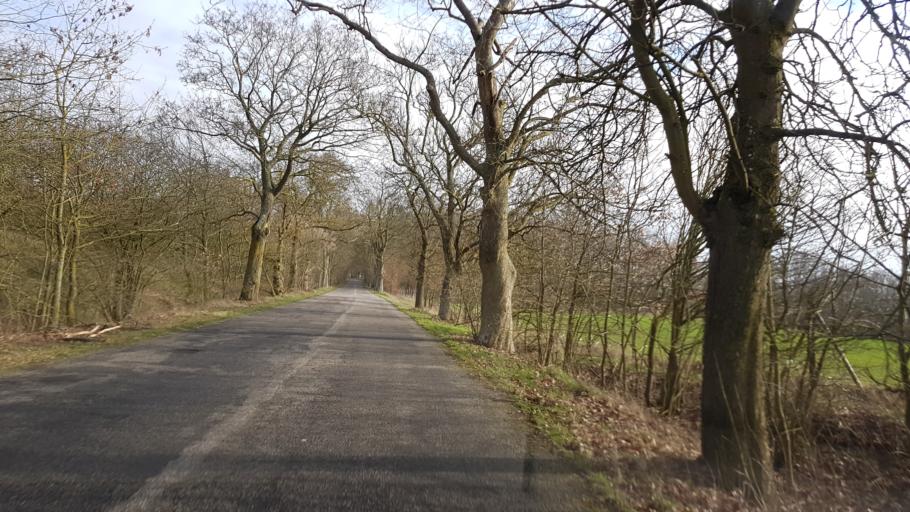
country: PL
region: West Pomeranian Voivodeship
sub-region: Powiat policki
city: Dobra
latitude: 53.5392
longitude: 14.3154
